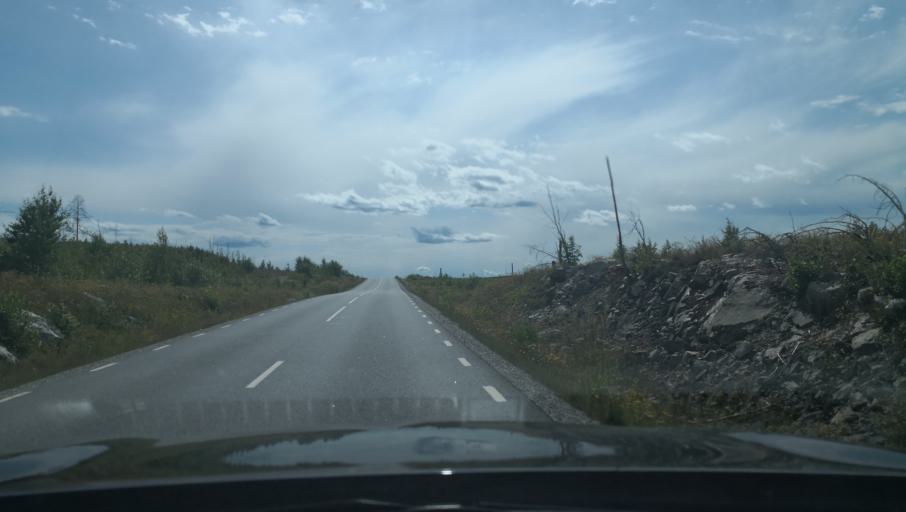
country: SE
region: Vaestmanland
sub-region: Norbergs Kommun
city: Norberg
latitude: 59.9859
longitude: 16.0543
